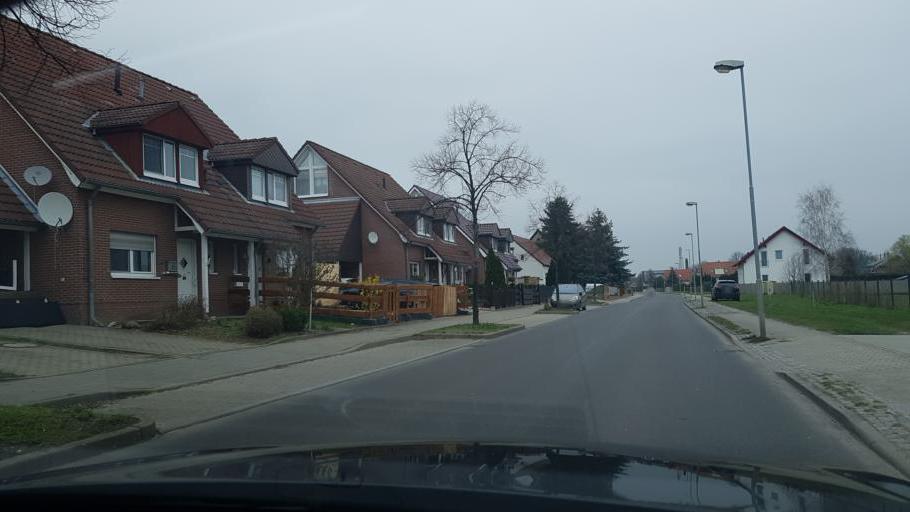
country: DE
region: Brandenburg
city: Mittenwalde
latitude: 52.2848
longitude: 13.5406
